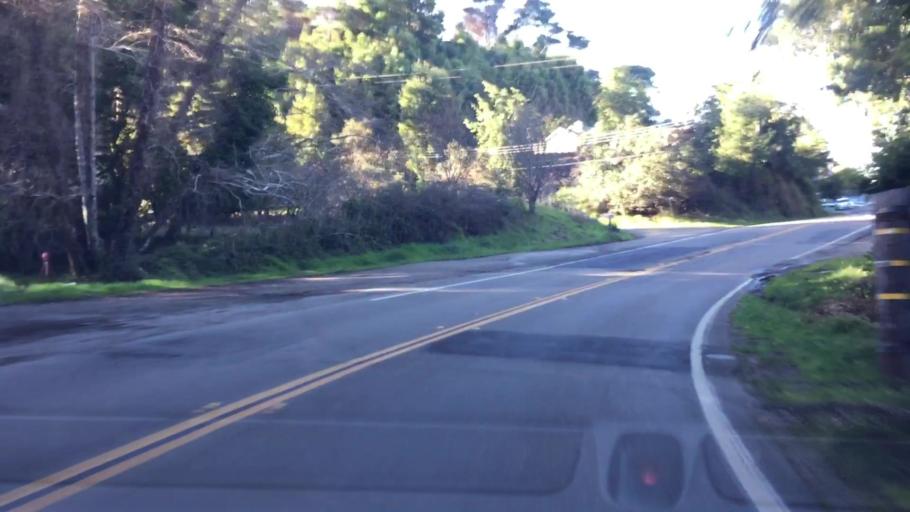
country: US
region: California
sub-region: Marin County
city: Inverness
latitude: 38.1053
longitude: -122.8618
